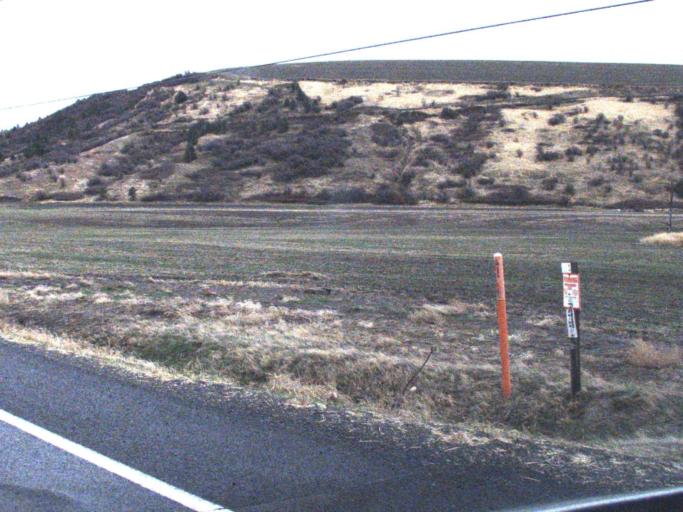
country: US
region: Washington
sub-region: Columbia County
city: Dayton
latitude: 46.2879
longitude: -118.0420
